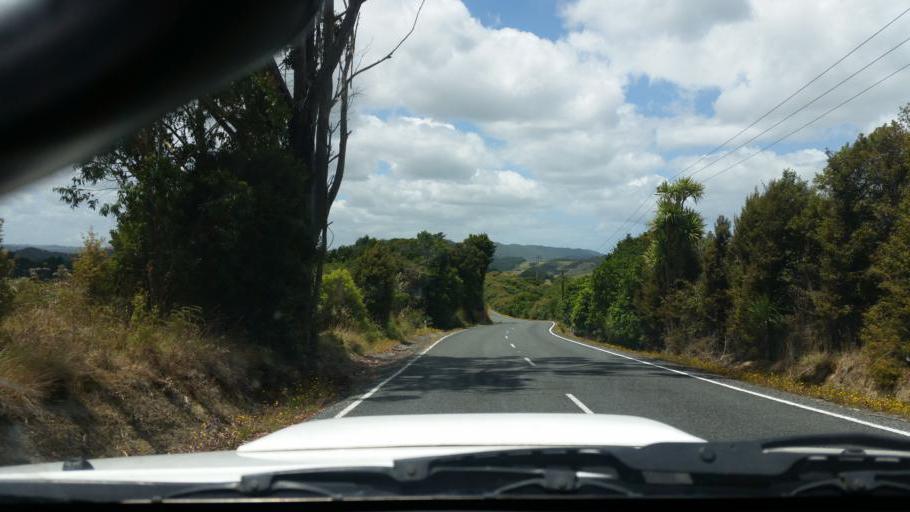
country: NZ
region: Northland
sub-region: Whangarei
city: Ruakaka
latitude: -36.0642
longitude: 174.2688
